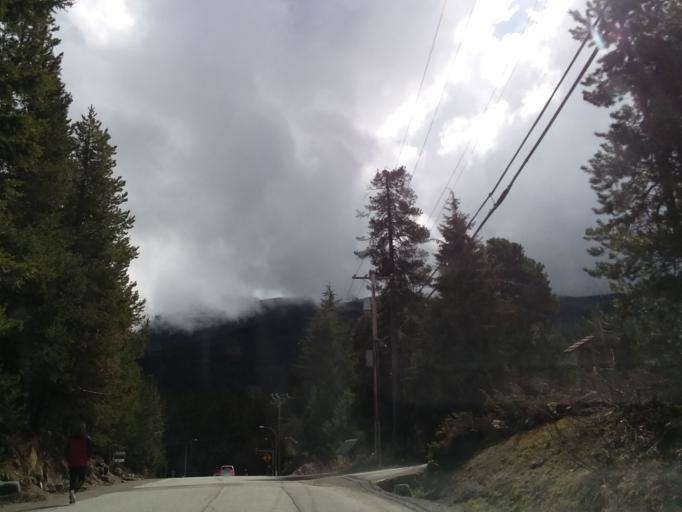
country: CA
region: British Columbia
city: Whistler
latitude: 50.0913
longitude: -123.0076
